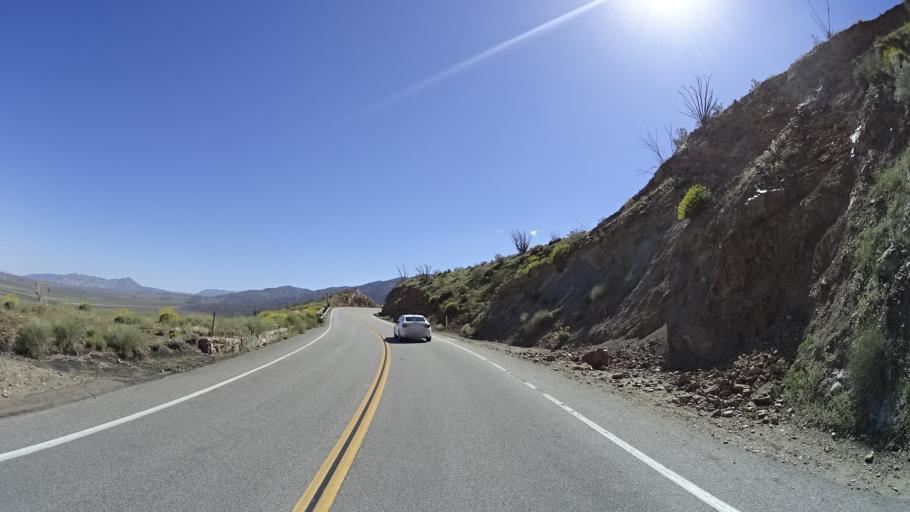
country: US
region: California
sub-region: San Diego County
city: Borrego Springs
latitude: 33.2370
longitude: -116.4083
